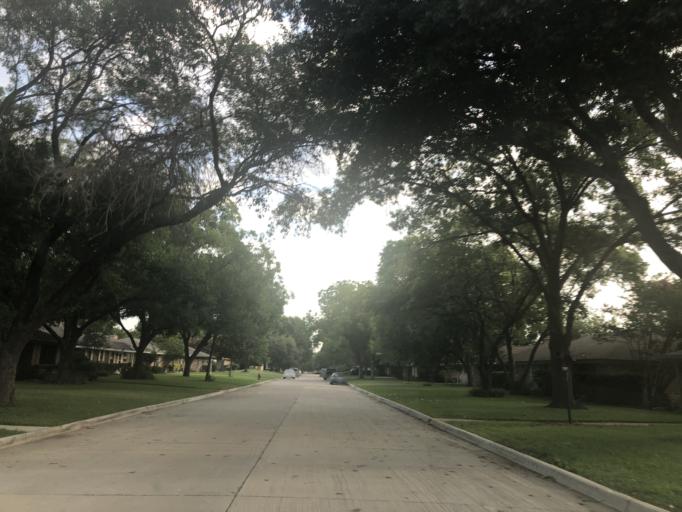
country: US
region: Texas
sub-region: Dallas County
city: Grand Prairie
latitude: 32.7652
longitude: -97.0135
